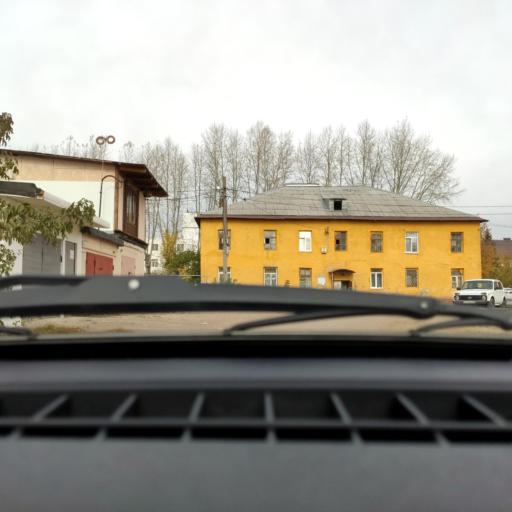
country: RU
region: Bashkortostan
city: Ufa
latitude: 54.7920
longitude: 56.1405
